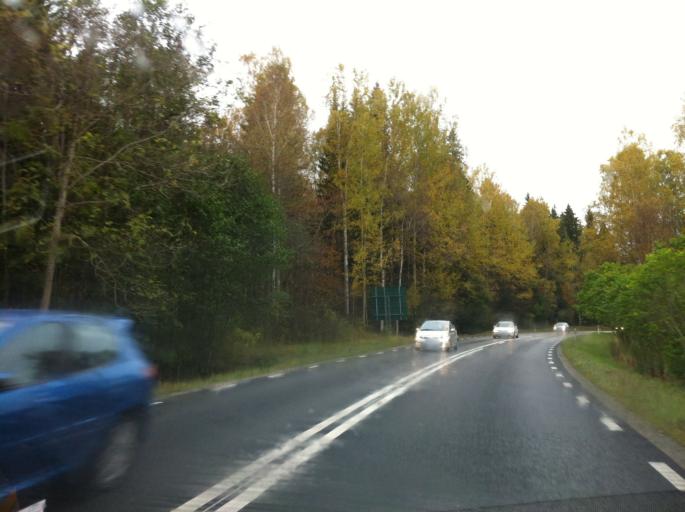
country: SE
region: OErebro
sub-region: Lindesbergs Kommun
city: Stora
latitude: 59.6638
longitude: 15.0990
